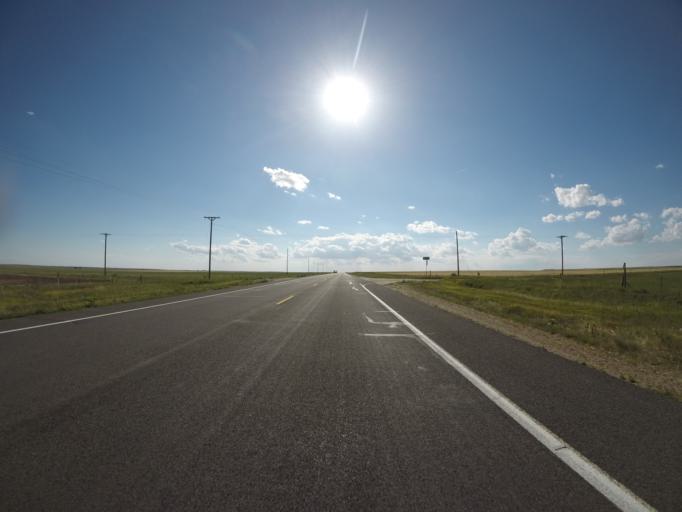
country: US
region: Colorado
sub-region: Morgan County
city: Fort Morgan
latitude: 40.6110
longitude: -103.7719
